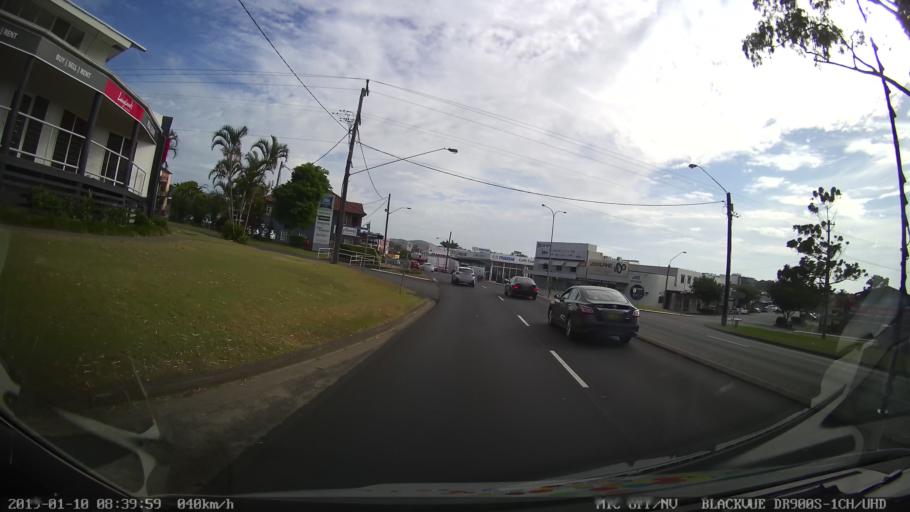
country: AU
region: New South Wales
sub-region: Coffs Harbour
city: Coffs Harbour
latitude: -30.2987
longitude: 153.1121
